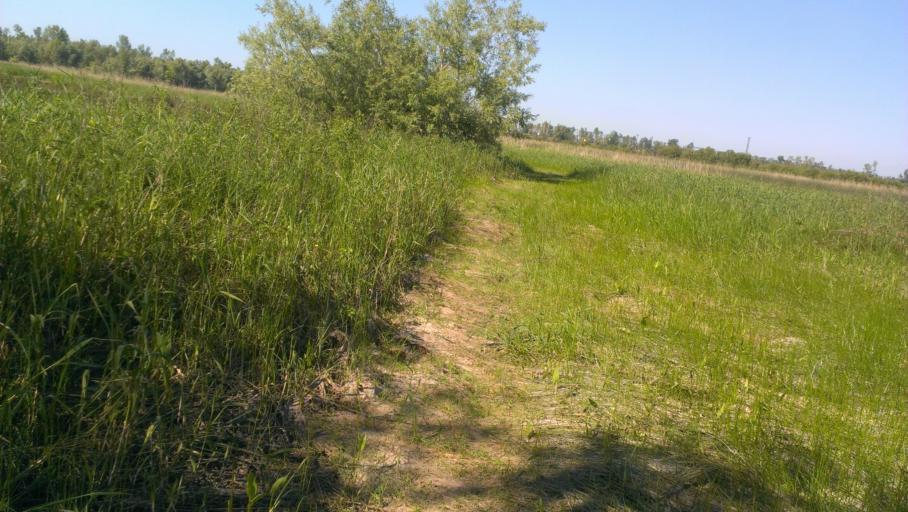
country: RU
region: Altai Krai
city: Novoaltaysk
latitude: 53.3645
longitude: 83.8614
